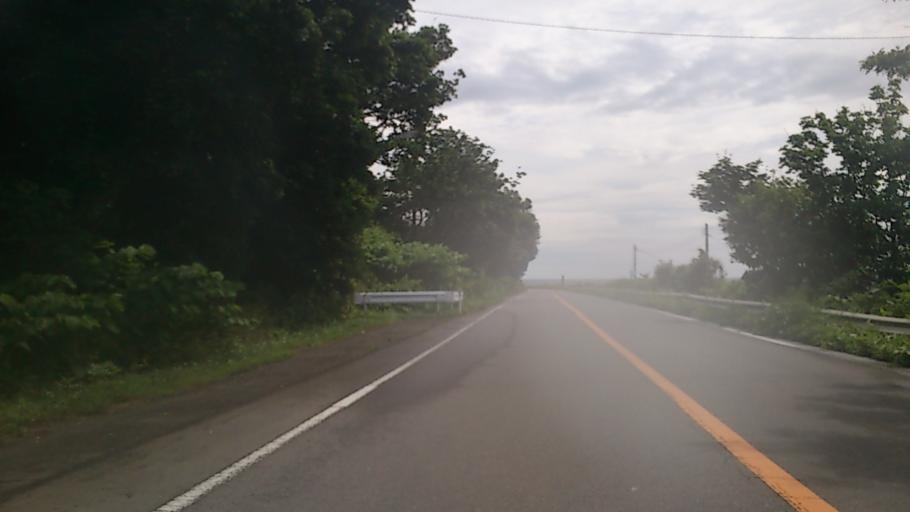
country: JP
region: Akita
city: Noshiromachi
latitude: 40.4482
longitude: 139.9415
